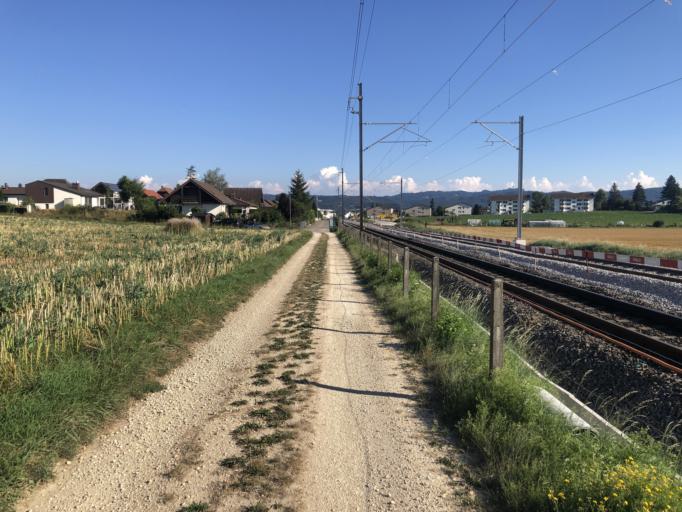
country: CH
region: Bern
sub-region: Bern-Mittelland District
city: Jegenstorf
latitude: 47.0593
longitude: 7.5081
